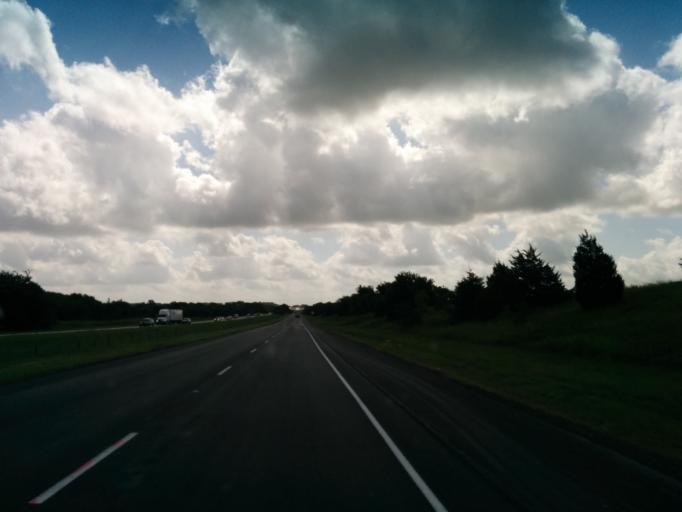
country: US
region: Texas
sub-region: Fayette County
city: Schulenburg
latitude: 29.6959
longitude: -96.8808
